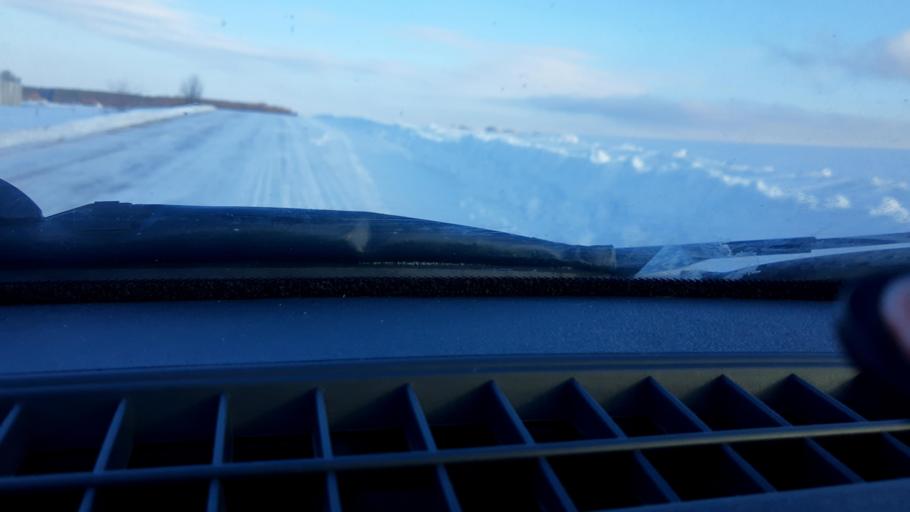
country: RU
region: Bashkortostan
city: Birsk
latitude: 55.1549
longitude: 55.6599
